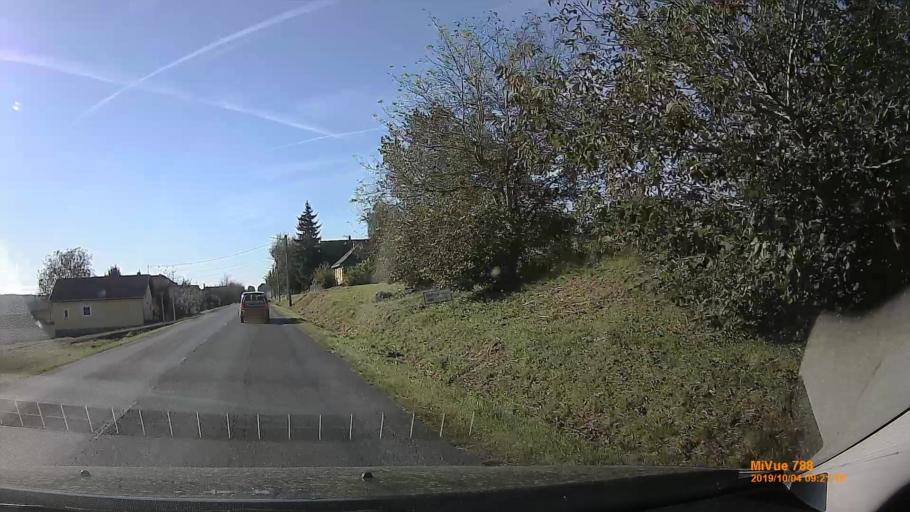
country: HU
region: Somogy
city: Karad
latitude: 46.5565
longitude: 17.8108
